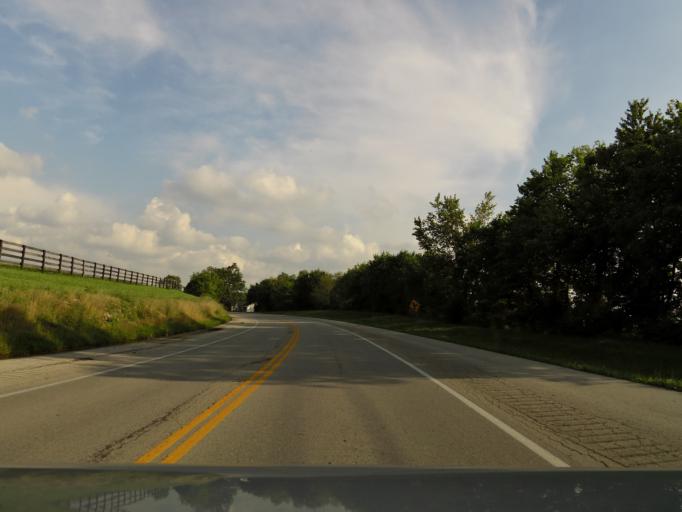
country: US
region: Kentucky
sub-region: Harrison County
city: Cynthiana
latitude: 38.3009
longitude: -84.3064
